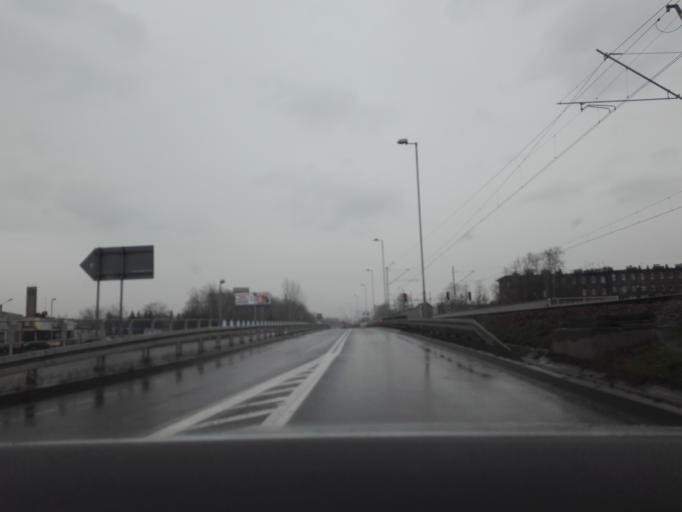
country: PL
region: Silesian Voivodeship
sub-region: Katowice
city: Katowice
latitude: 50.2641
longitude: 18.9885
